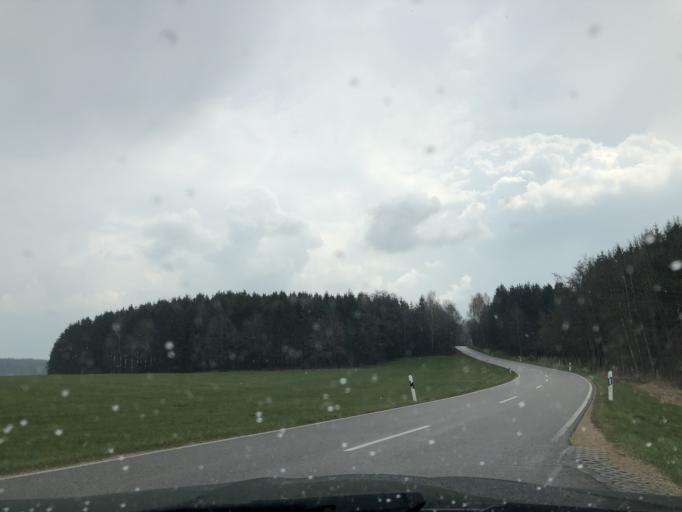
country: DE
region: Bavaria
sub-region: Upper Bavaria
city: Wolfersdorf
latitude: 48.4966
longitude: 11.6897
